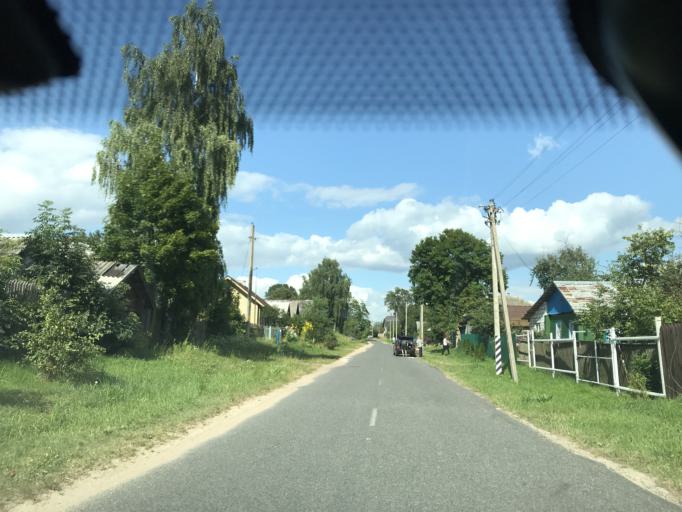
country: BY
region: Mogilev
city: Poselok Voskhod
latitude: 53.7885
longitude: 30.3574
